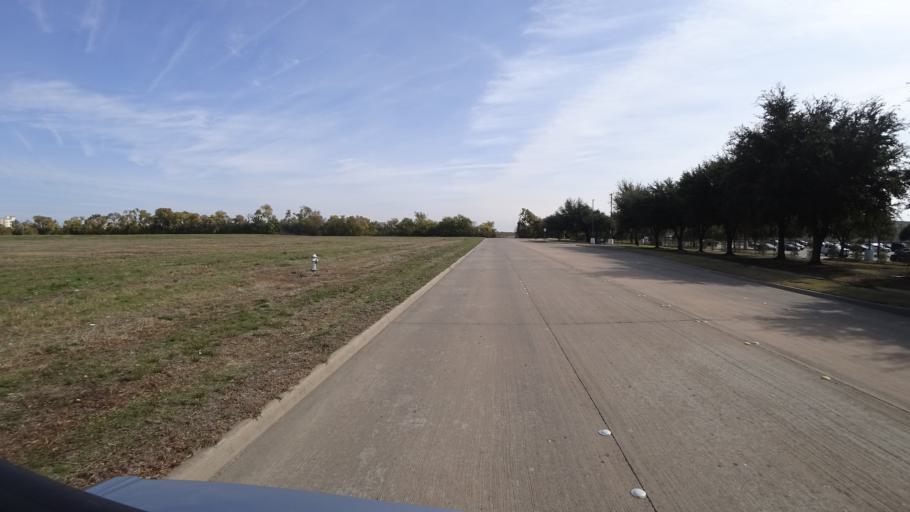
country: US
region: Texas
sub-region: Denton County
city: The Colony
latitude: 33.0658
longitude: -96.8729
